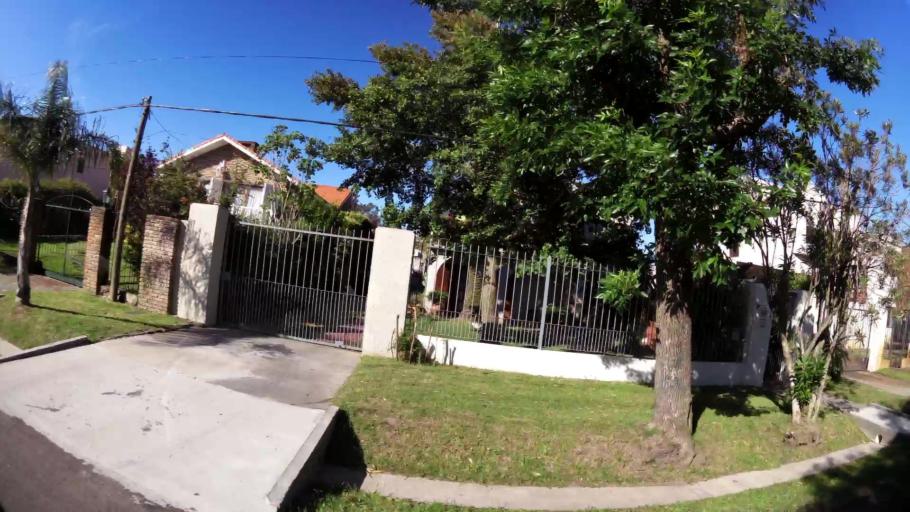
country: UY
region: Canelones
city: Barra de Carrasco
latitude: -34.8733
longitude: -56.0224
